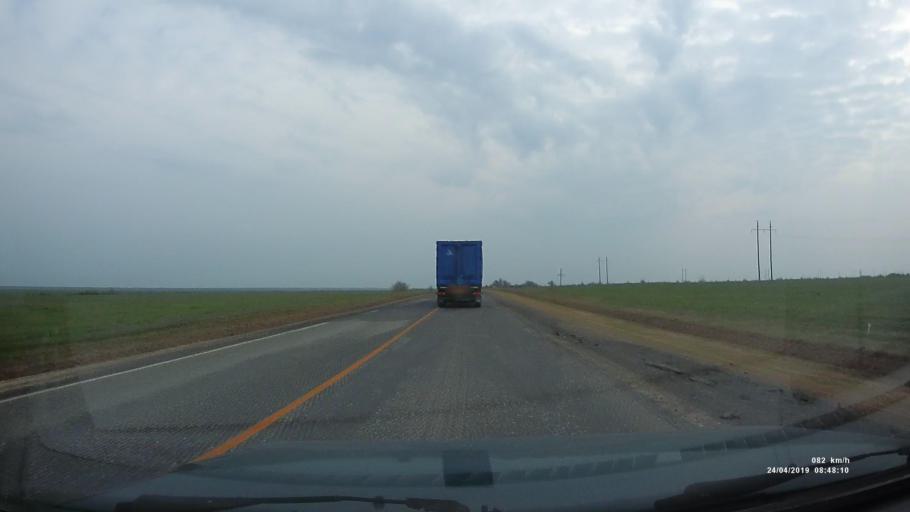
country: RU
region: Kalmykiya
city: Arshan'
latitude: 46.2496
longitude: 44.1053
